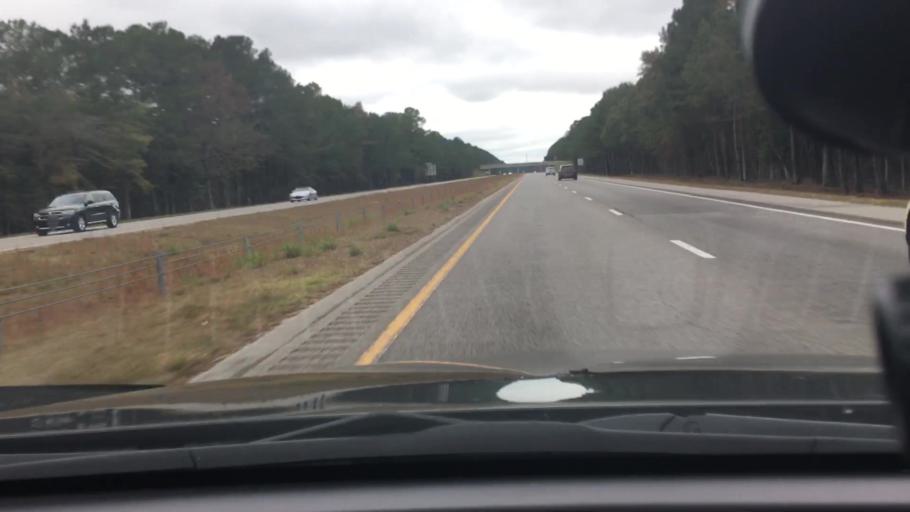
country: US
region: North Carolina
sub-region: Wilson County
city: Wilson
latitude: 35.6704
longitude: -77.7758
